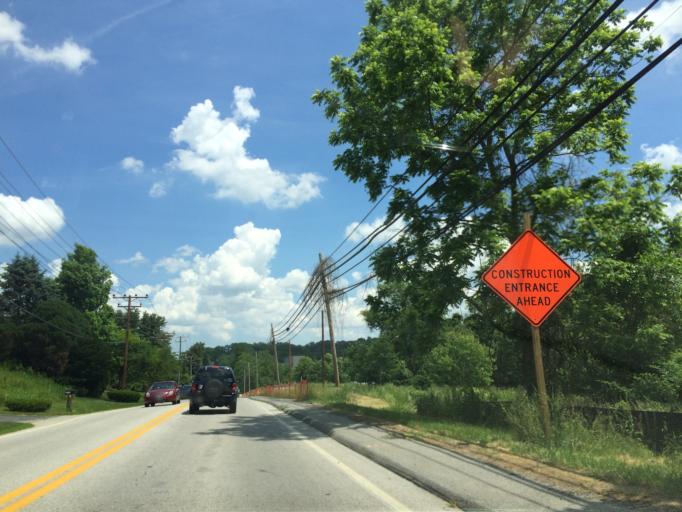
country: US
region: Maryland
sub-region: Howard County
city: Columbia
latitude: 39.2743
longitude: -76.8447
